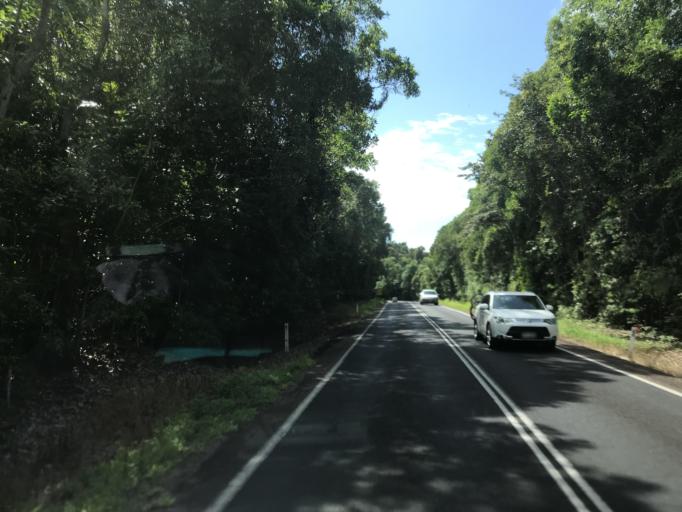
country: AU
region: Queensland
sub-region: Cassowary Coast
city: Innisfail
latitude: -17.8659
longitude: 146.0669
